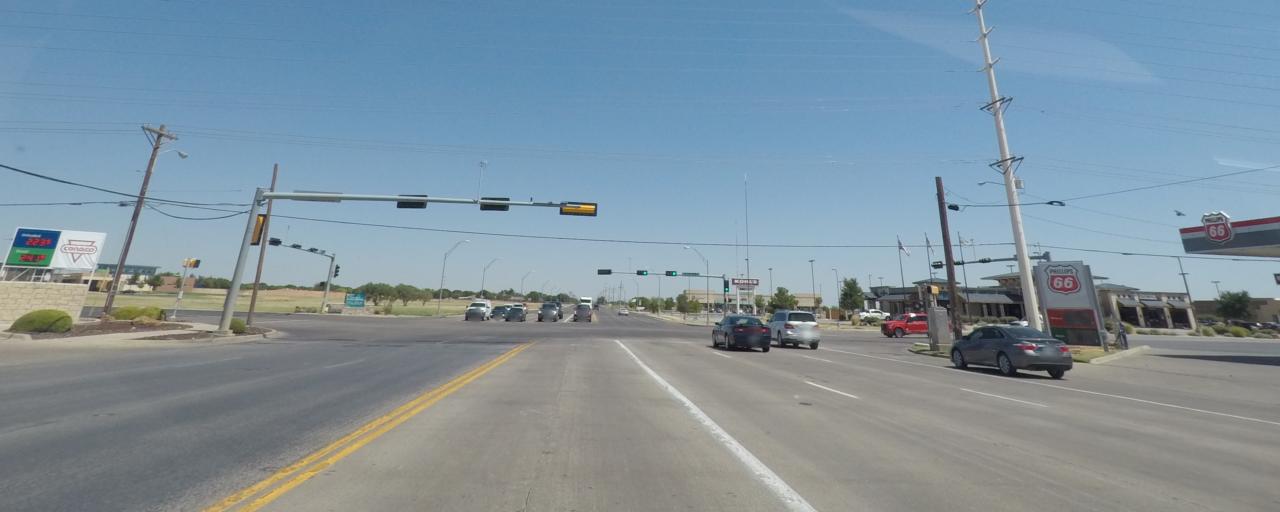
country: US
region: Texas
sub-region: Lubbock County
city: Lubbock
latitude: 33.5053
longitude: -101.8884
